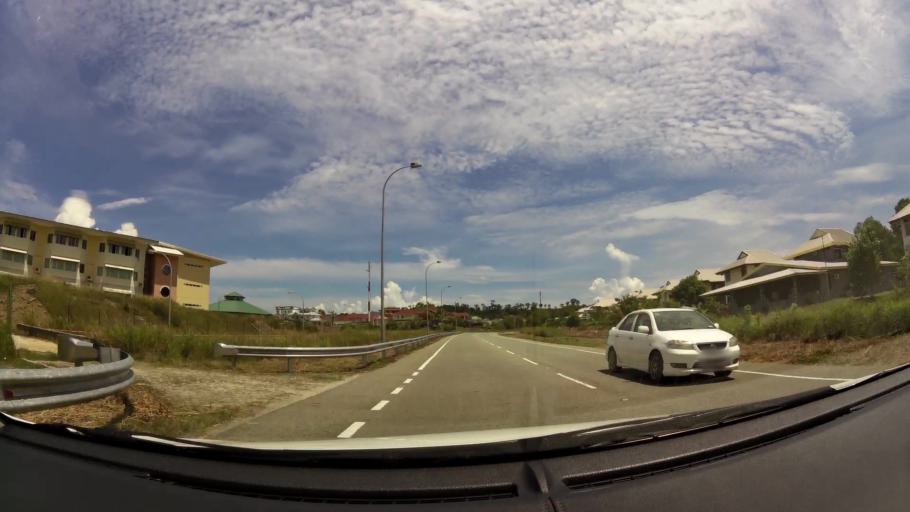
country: BN
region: Brunei and Muara
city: Bandar Seri Begawan
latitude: 4.9652
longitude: 114.9043
